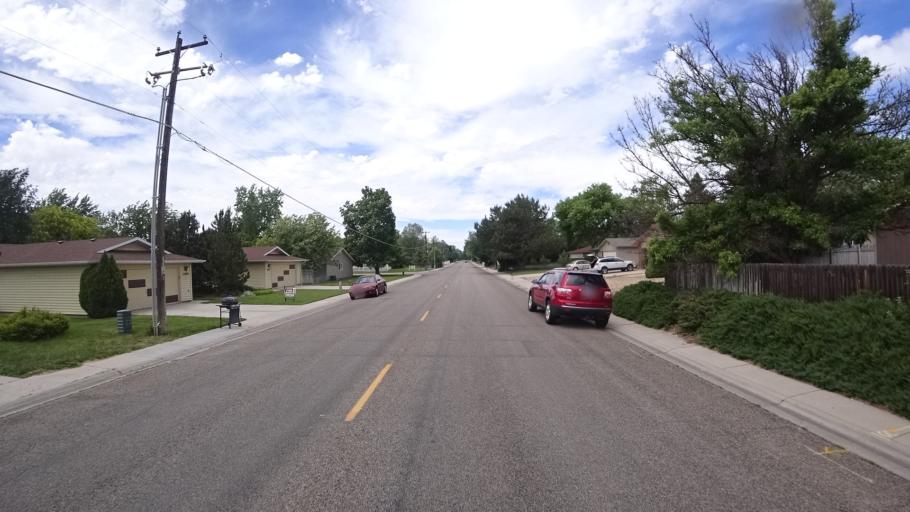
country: US
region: Idaho
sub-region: Ada County
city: Eagle
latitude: 43.6412
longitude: -116.3177
